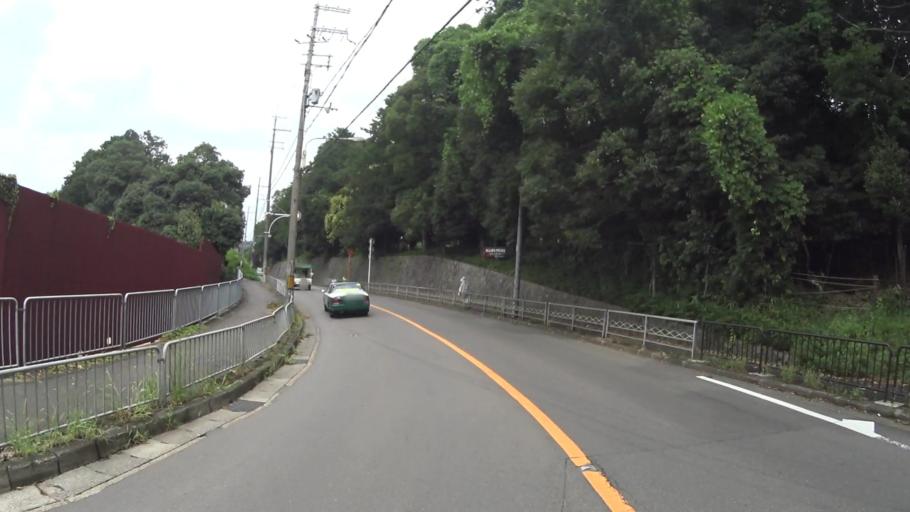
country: JP
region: Kyoto
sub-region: Kyoto-shi
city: Kamigyo-ku
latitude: 35.0649
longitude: 135.7506
